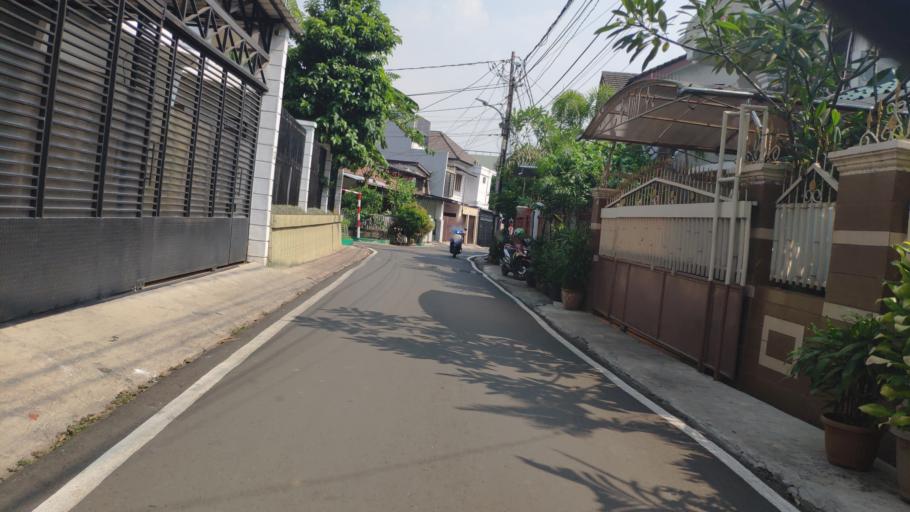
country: ID
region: Jakarta Raya
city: Jakarta
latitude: -6.2515
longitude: 106.7952
